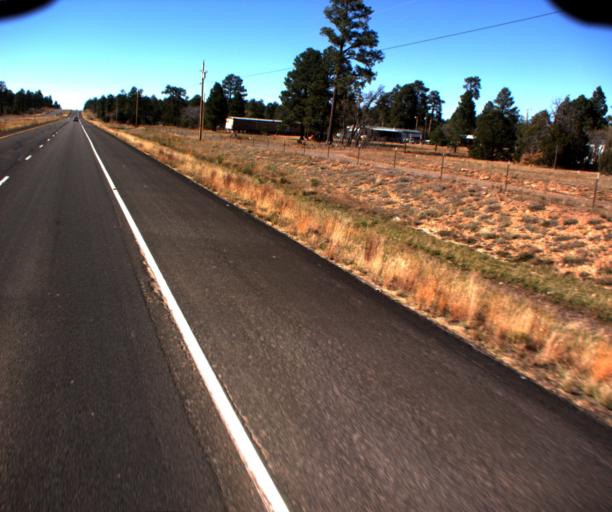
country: US
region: Arizona
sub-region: Apache County
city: Saint Michaels
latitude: 35.6760
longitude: -109.1906
